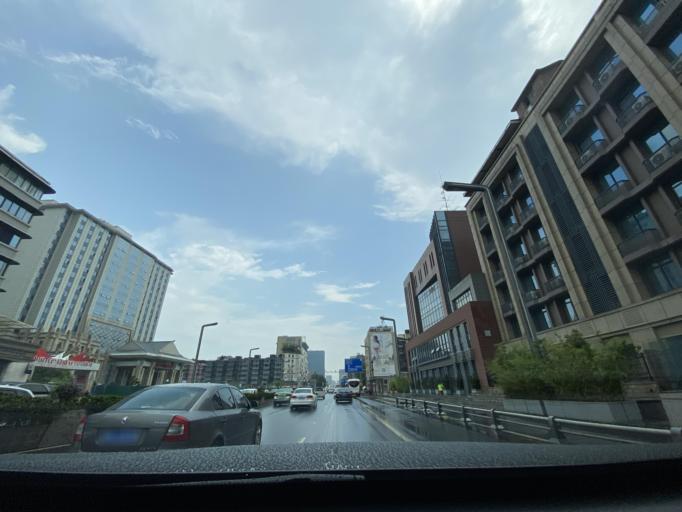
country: CN
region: Sichuan
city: Chengdu
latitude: 30.6404
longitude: 104.0734
